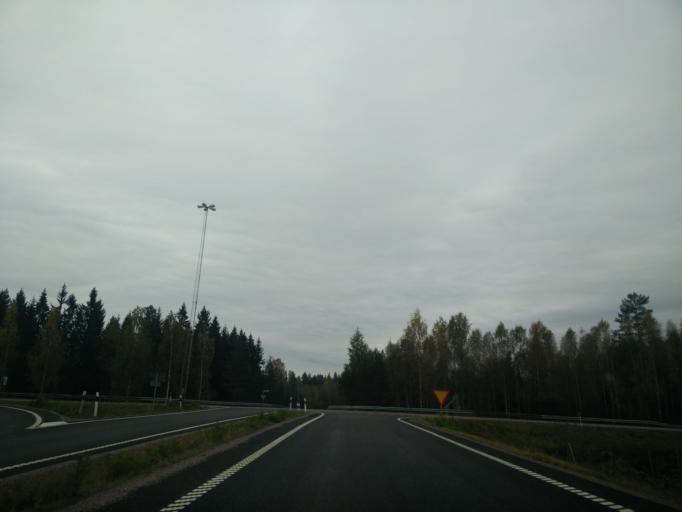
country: SE
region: Gaevleborg
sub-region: Gavle Kommun
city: Norrsundet
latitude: 60.9024
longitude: 17.0147
